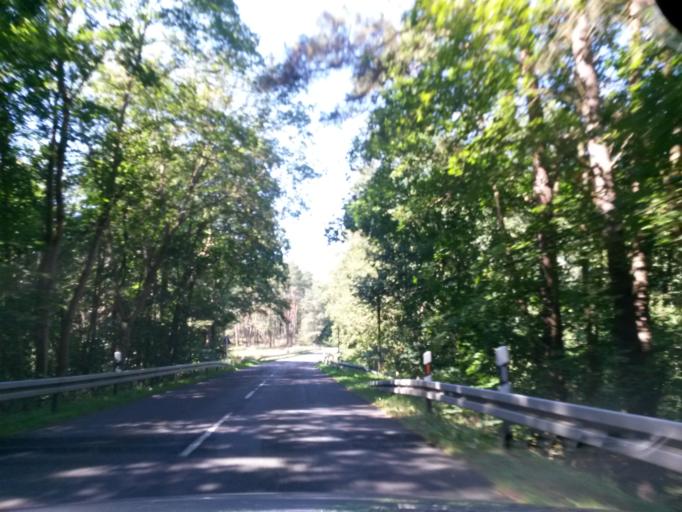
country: DE
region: Brandenburg
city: Lychen
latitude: 53.2198
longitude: 13.3386
